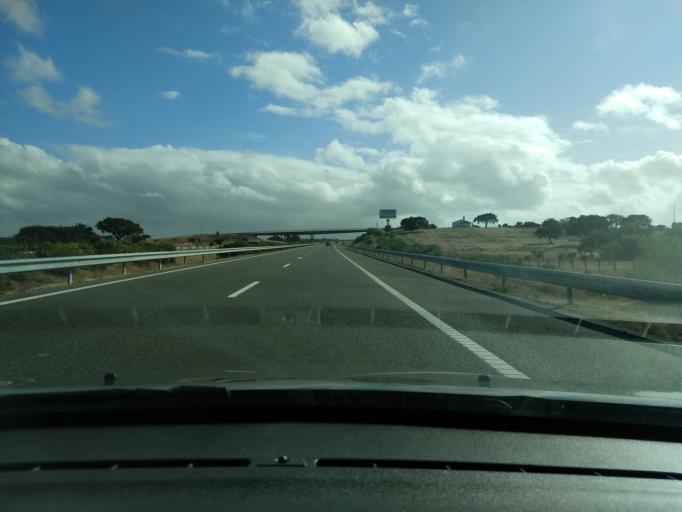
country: PT
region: Beja
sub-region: Ourique
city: Ourique
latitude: 37.6516
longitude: -8.1559
